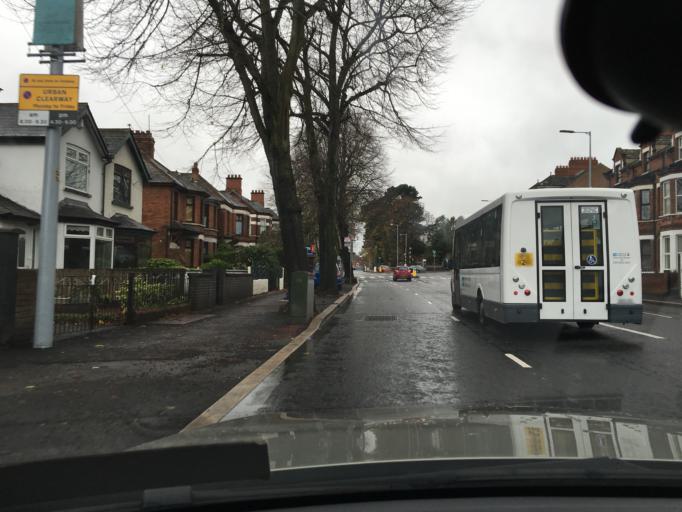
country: GB
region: Northern Ireland
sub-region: City of Belfast
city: Belfast
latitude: 54.5893
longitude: -5.9691
